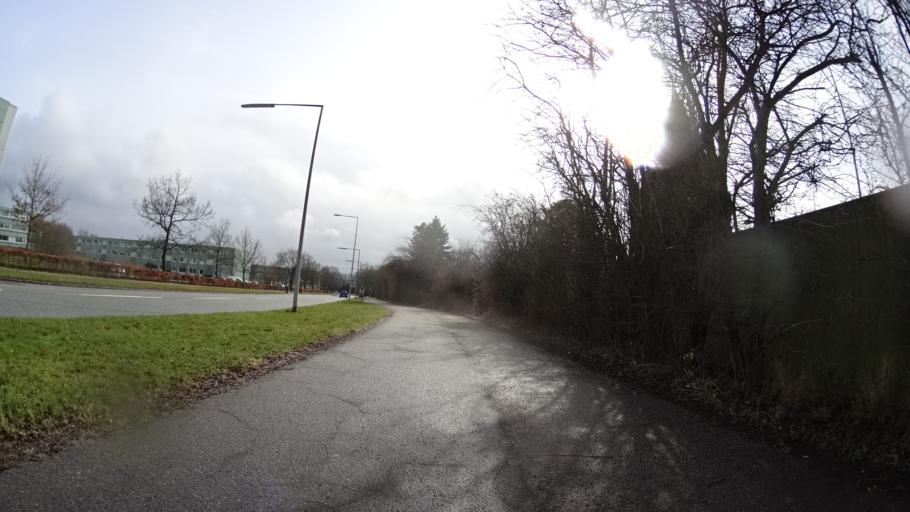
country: DK
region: Central Jutland
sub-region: Arhus Kommune
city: Arhus
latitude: 56.1697
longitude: 10.1721
